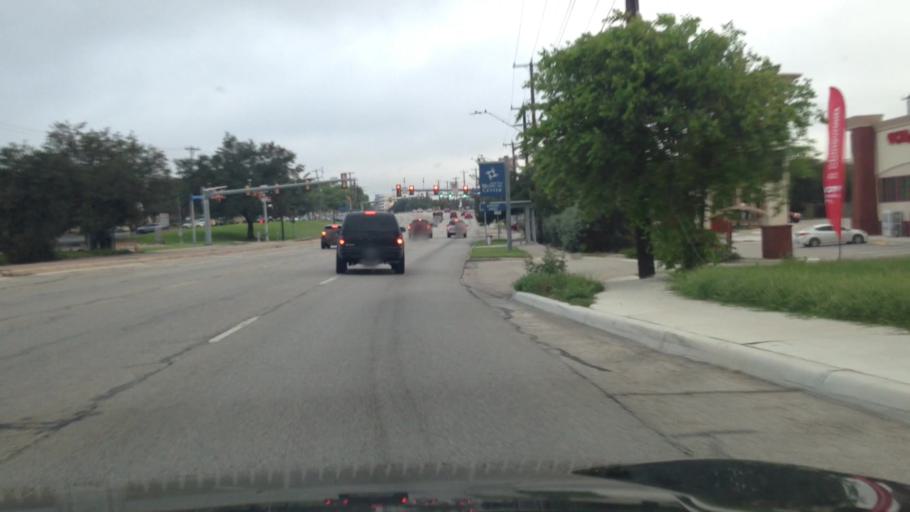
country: US
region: Texas
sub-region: Bexar County
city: Balcones Heights
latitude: 29.4952
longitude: -98.5551
